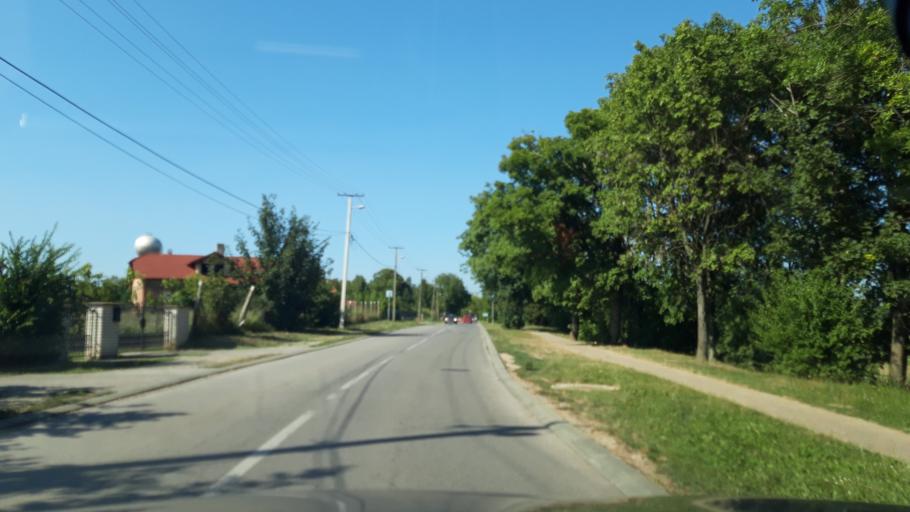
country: RS
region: Autonomna Pokrajina Vojvodina
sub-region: Sremski Okrug
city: Ruma
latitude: 45.0242
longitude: 19.8209
